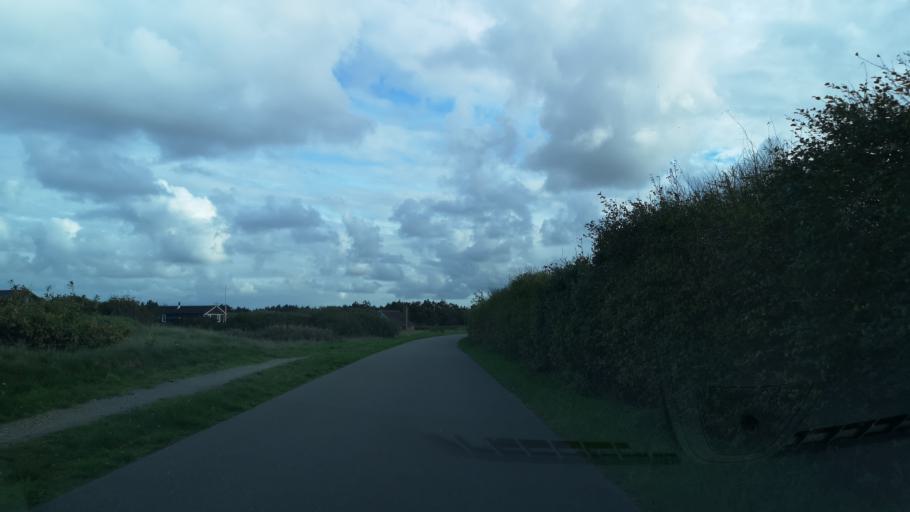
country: DK
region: Central Jutland
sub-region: Ringkobing-Skjern Kommune
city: Ringkobing
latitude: 56.1395
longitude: 8.1330
